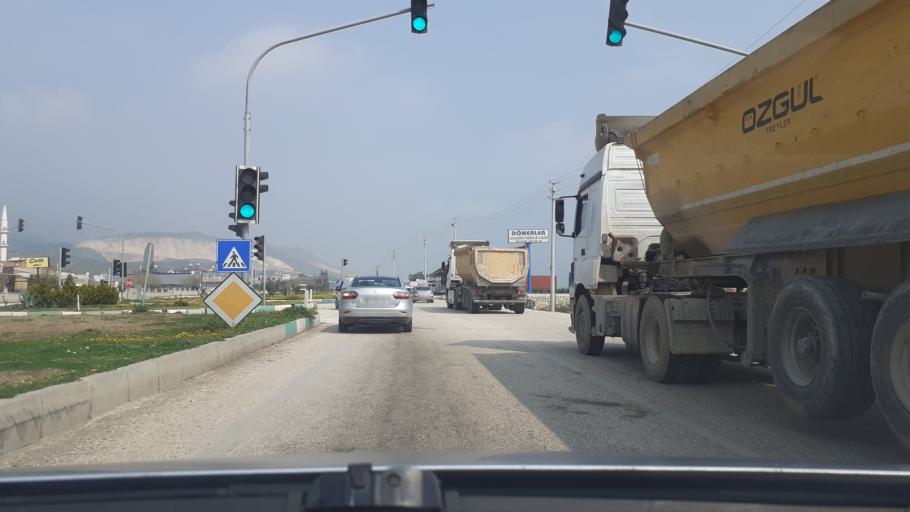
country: TR
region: Hatay
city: Kirikhan
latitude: 36.5231
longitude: 36.3771
